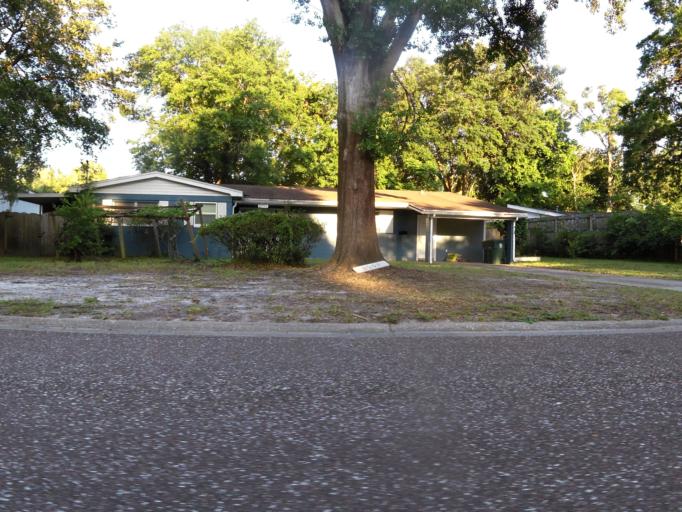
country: US
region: Florida
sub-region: Duval County
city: Jacksonville
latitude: 30.2335
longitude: -81.6155
